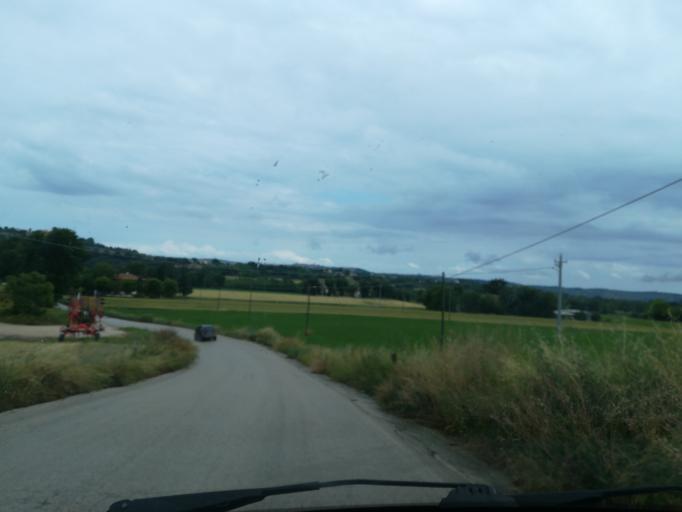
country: IT
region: The Marches
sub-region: Provincia di Macerata
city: Petriolo
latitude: 43.2302
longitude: 13.4625
